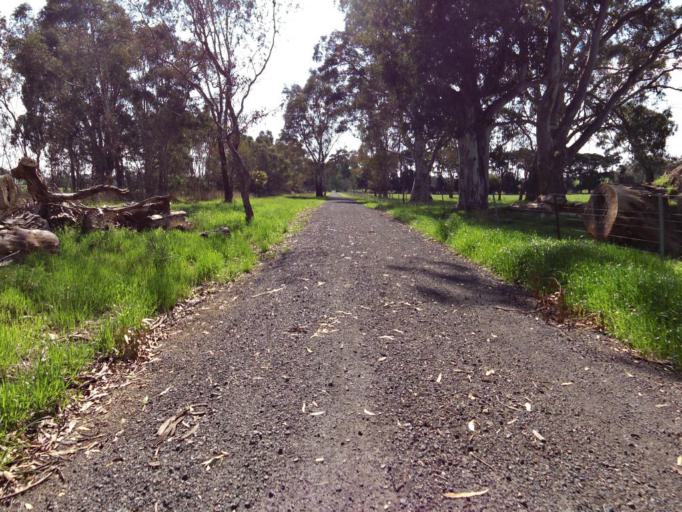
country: AU
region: Victoria
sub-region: Murrindindi
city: Alexandra
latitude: -37.1257
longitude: 145.5984
